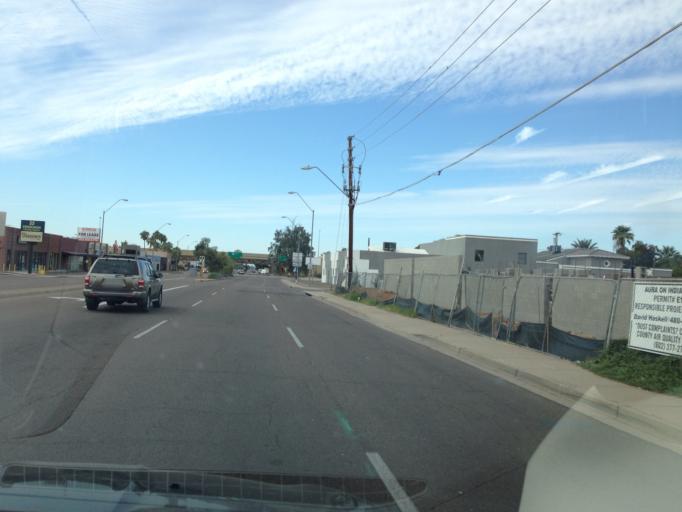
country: US
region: Arizona
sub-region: Maricopa County
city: Phoenix
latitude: 33.4948
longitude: -112.0403
